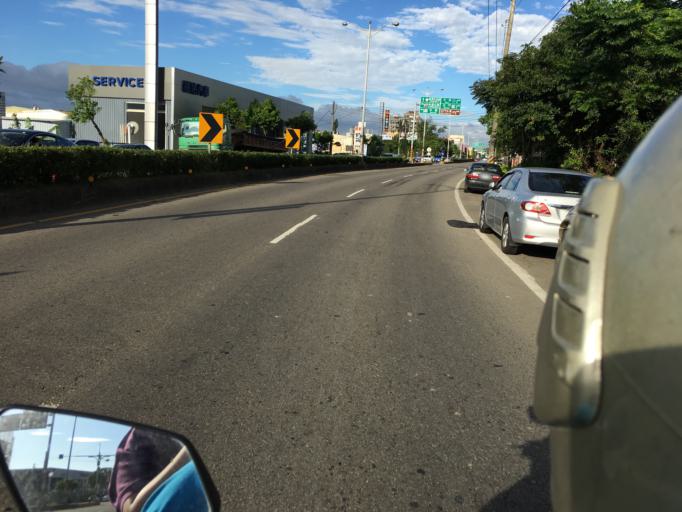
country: TW
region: Taiwan
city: Daxi
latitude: 24.8673
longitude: 121.2110
